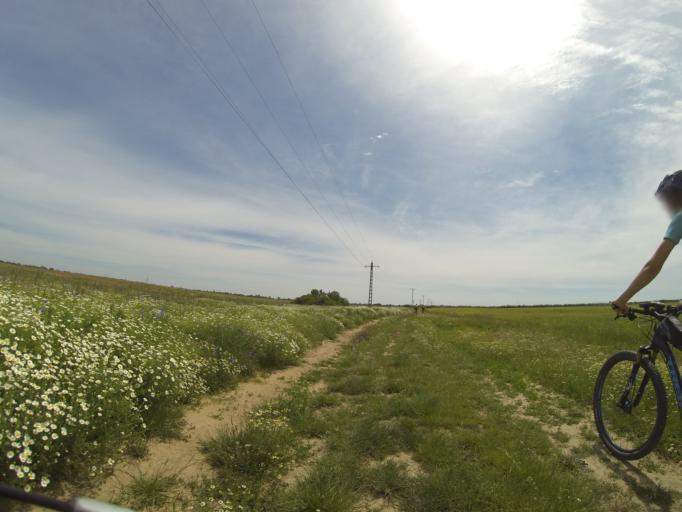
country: RO
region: Dolj
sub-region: Comuna Ghindeni
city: Ghindeni
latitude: 44.2049
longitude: 23.9625
